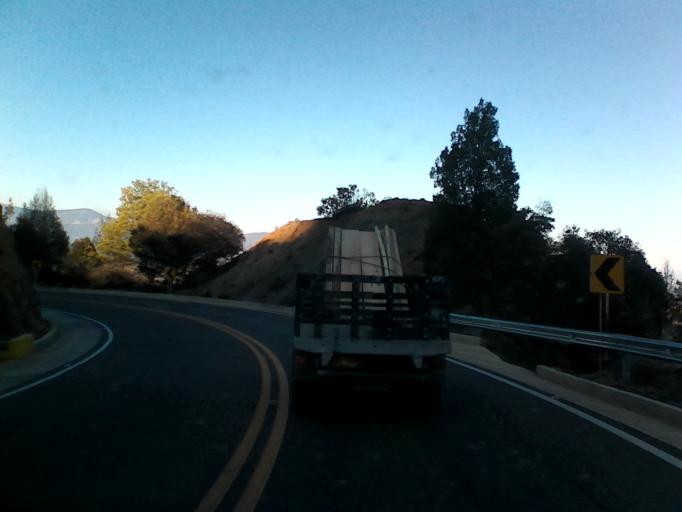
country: CO
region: Boyaca
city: Cucaita
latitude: 5.5566
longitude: -73.4320
